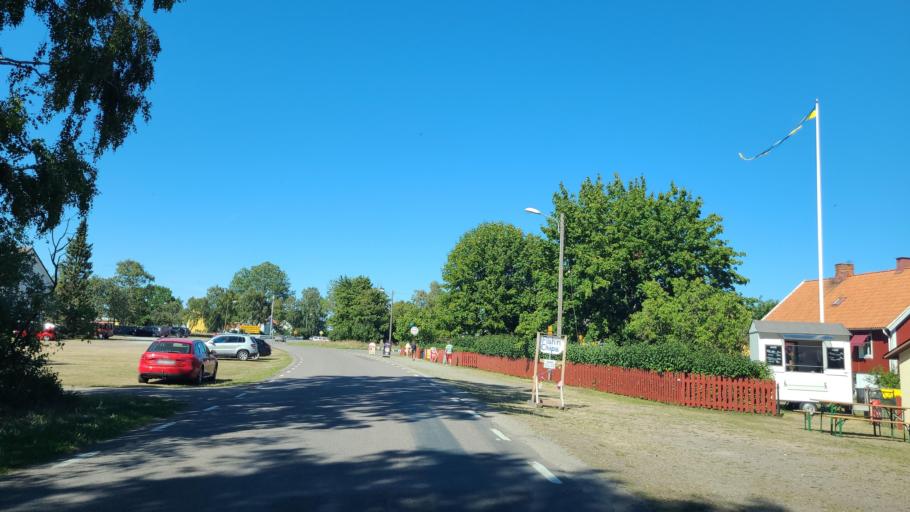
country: SE
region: Kalmar
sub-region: Borgholms Kommun
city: Borgholm
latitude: 56.8437
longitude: 16.7946
